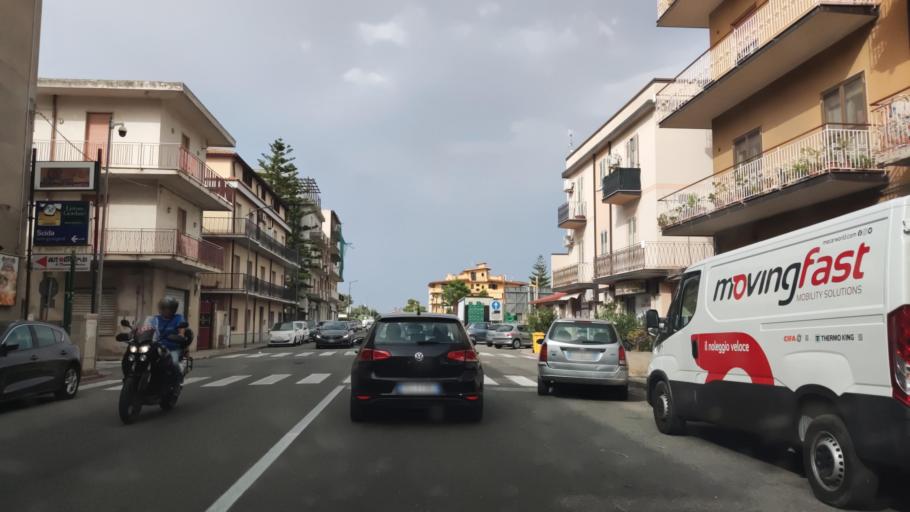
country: IT
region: Calabria
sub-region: Provincia di Reggio Calabria
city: Locri
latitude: 38.2409
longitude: 16.2710
